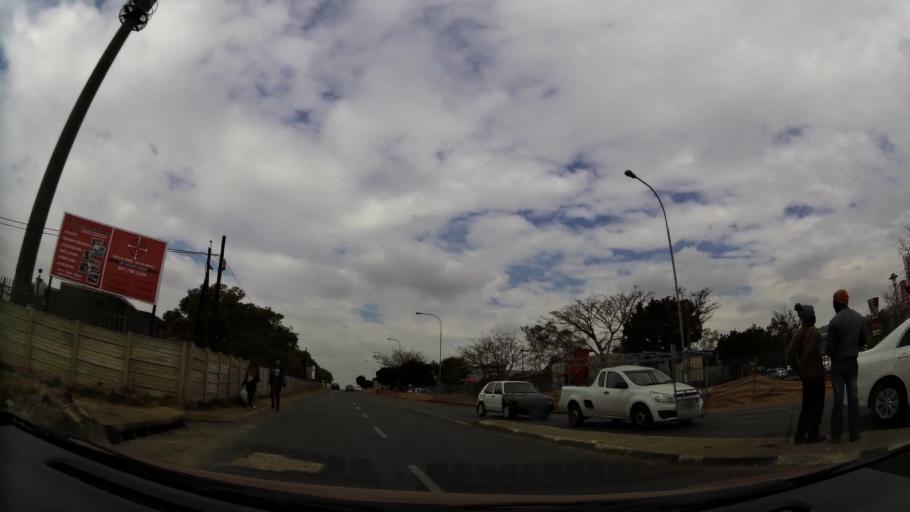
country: ZA
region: Gauteng
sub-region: West Rand District Municipality
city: Muldersdriseloop
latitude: -26.0894
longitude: 27.8711
